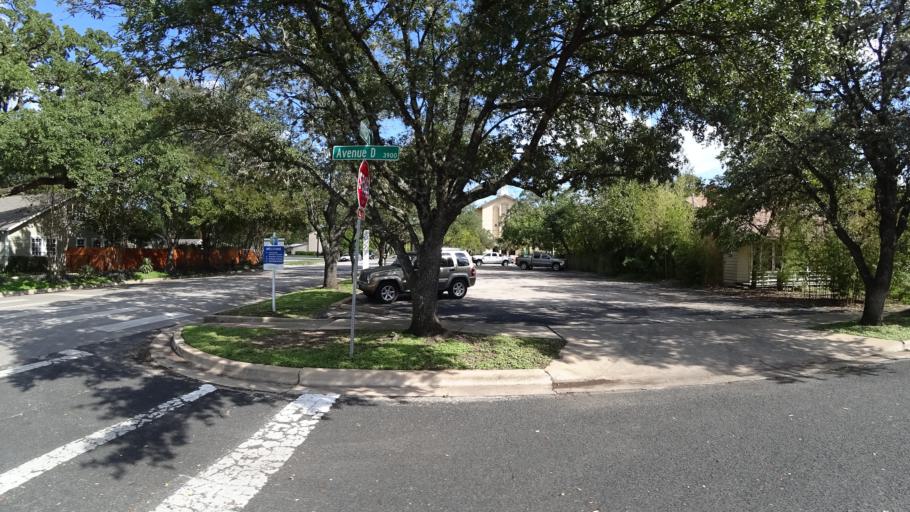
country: US
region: Texas
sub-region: Travis County
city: Austin
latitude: 30.3035
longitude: -97.7330
